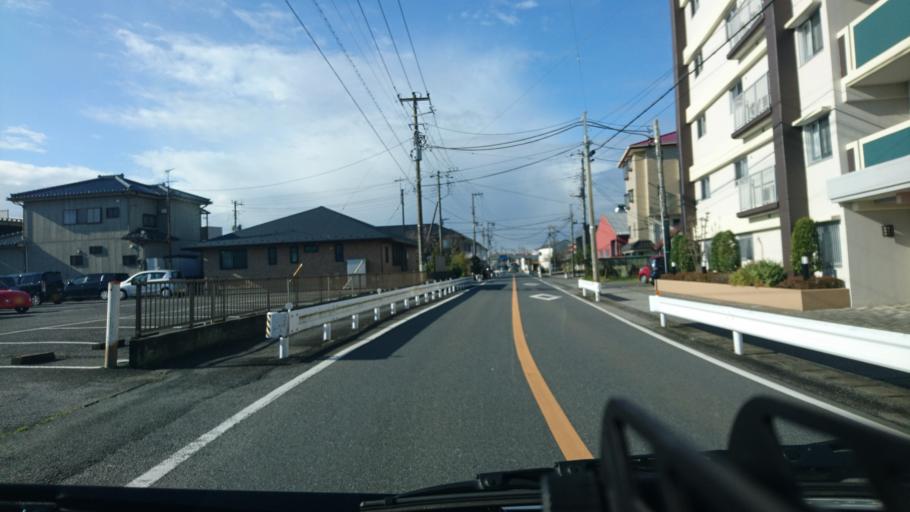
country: JP
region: Chiba
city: Kisarazu
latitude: 35.3704
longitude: 139.9233
